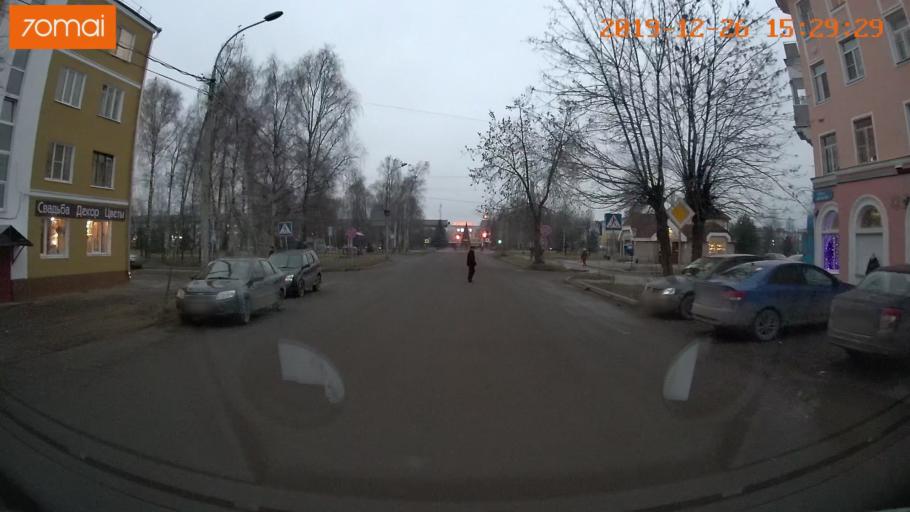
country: RU
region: Jaroslavl
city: Rybinsk
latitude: 58.0566
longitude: 38.8167
